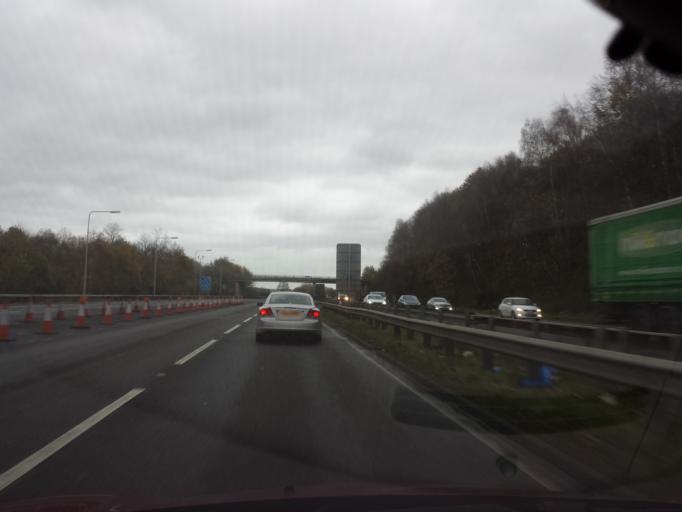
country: GB
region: England
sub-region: Surrey
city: Chertsey
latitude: 51.4011
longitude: -0.5287
